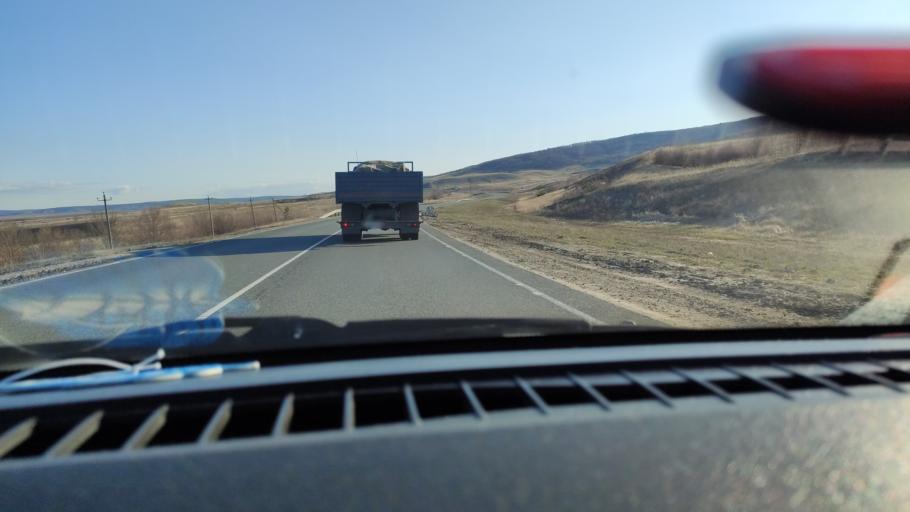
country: RU
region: Saratov
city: Alekseyevka
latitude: 52.3324
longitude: 47.9239
